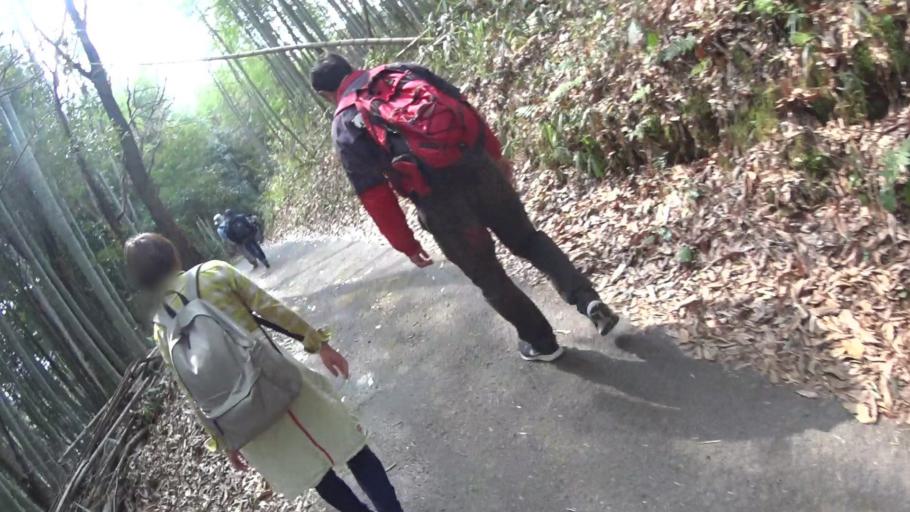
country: JP
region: Nara
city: Nara-shi
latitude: 34.7374
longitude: 135.8569
